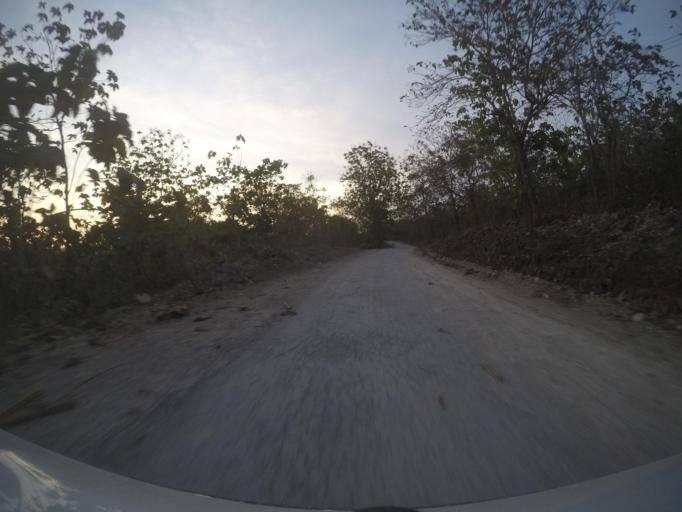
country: TL
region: Viqueque
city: Viqueque
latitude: -8.8951
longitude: 126.3880
